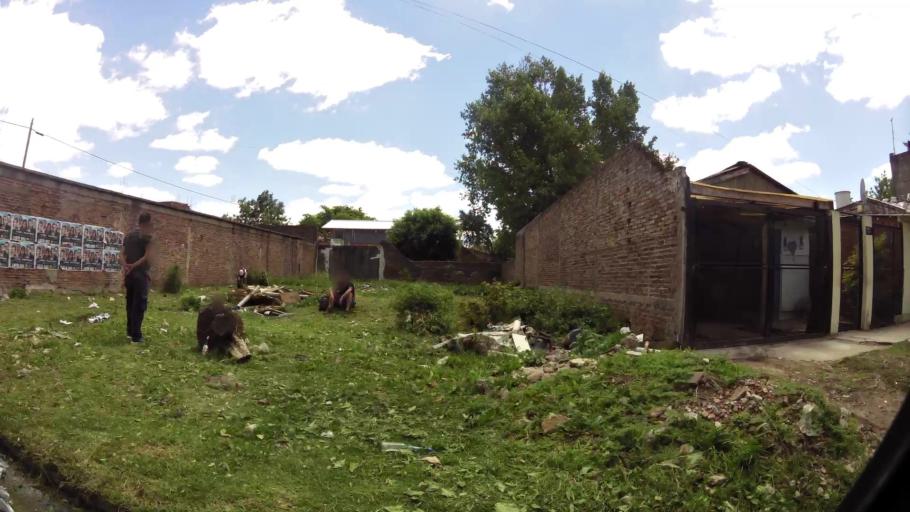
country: AR
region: Buenos Aires
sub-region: Partido de Lanus
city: Lanus
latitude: -34.7207
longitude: -58.4208
